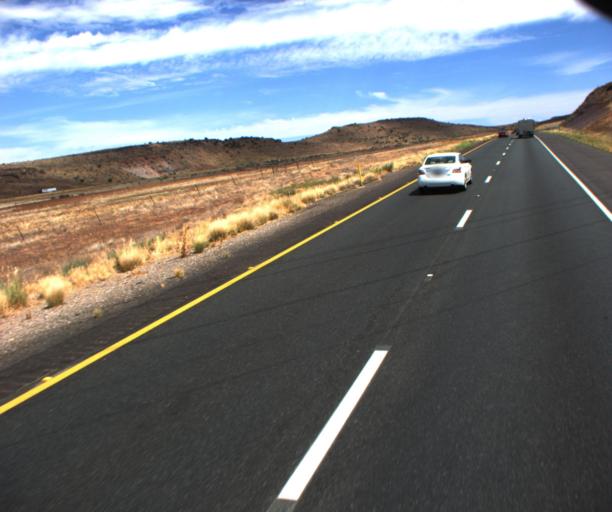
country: US
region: Arizona
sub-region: Yavapai County
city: Cordes Lakes
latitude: 34.4438
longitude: -112.0309
